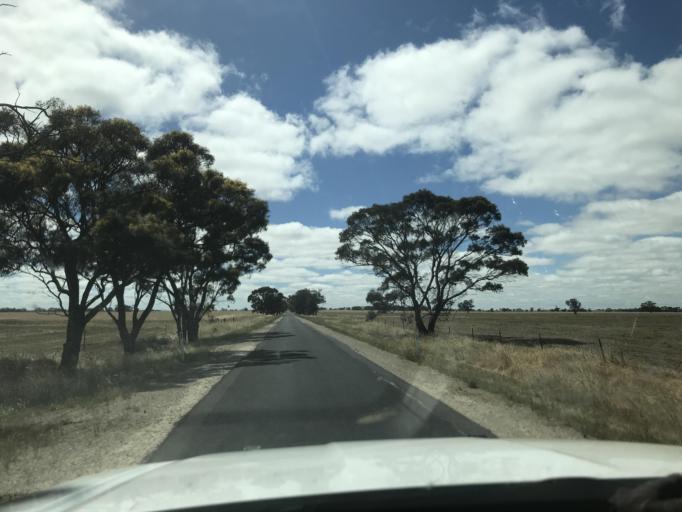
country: AU
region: South Australia
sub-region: Tatiara
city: Bordertown
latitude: -36.2774
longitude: 141.1043
